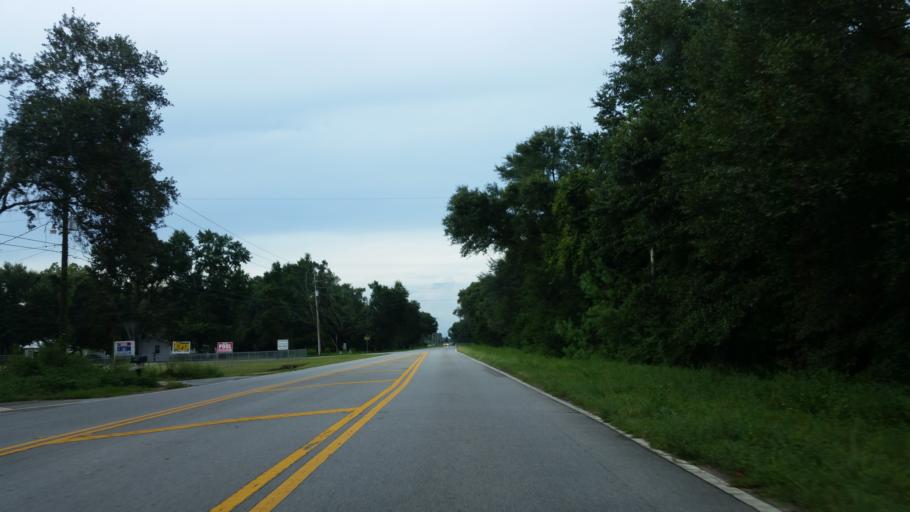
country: US
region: Florida
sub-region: Santa Rosa County
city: Pace
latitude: 30.5829
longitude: -87.1117
